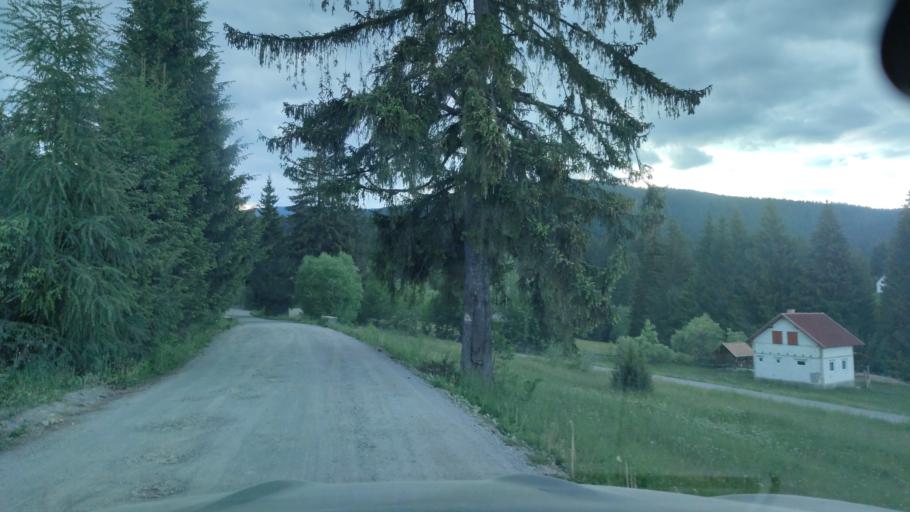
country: RO
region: Harghita
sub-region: Comuna Joseni
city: Joseni
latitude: 46.6722
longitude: 25.3699
